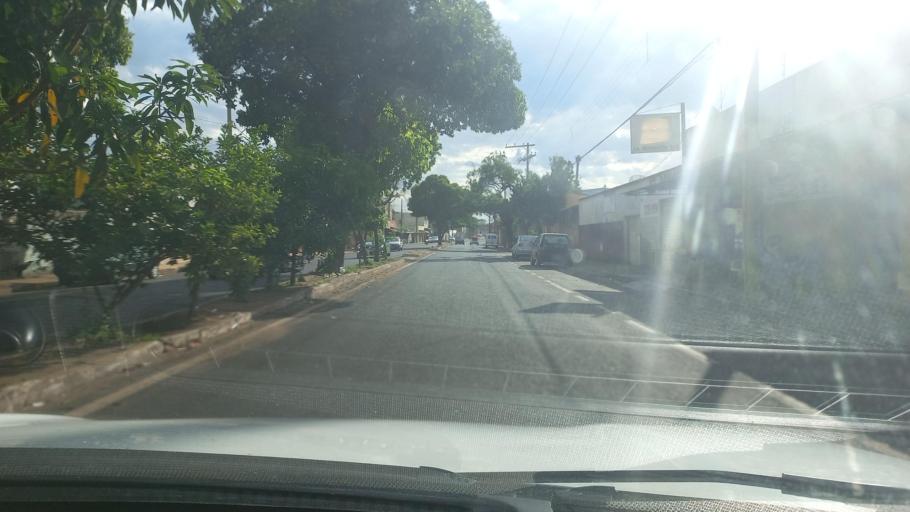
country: BR
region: Minas Gerais
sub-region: Uberaba
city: Uberaba
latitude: -19.7612
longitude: -47.9133
